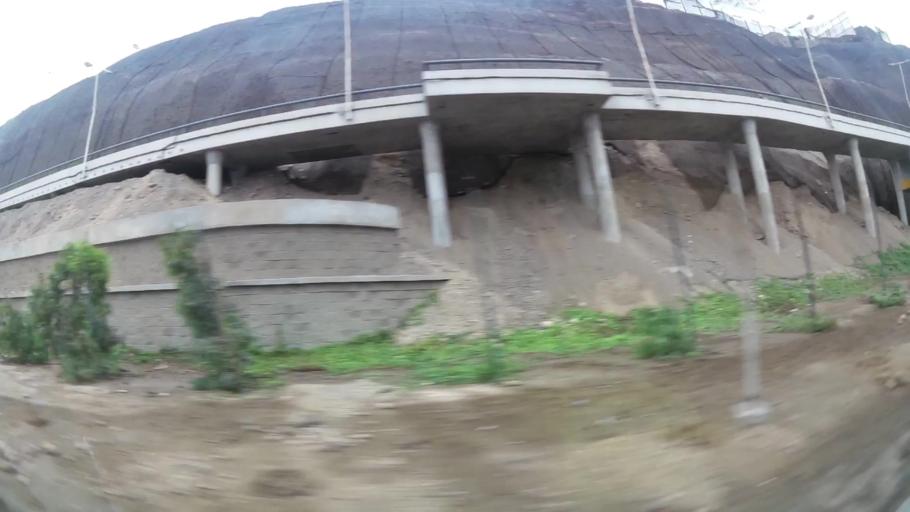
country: PE
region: Lima
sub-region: Lima
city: San Isidro
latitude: -12.0948
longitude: -77.0787
